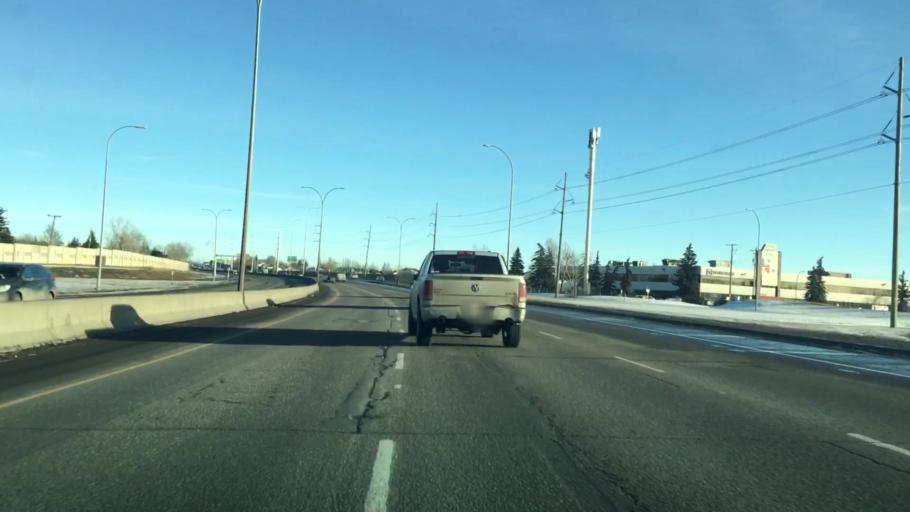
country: CA
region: Alberta
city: Calgary
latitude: 50.9802
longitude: -114.0145
